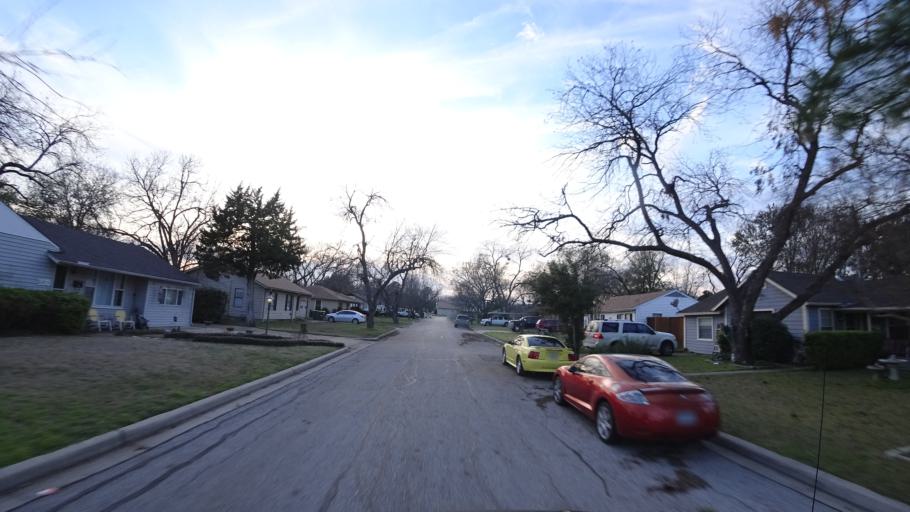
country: US
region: Texas
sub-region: Denton County
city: Lewisville
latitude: 33.0438
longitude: -96.9997
